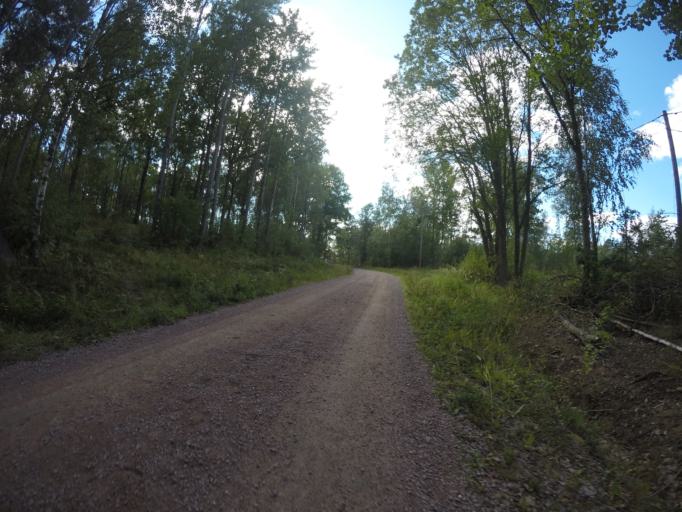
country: SE
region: Vaestmanland
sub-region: Hallstahammars Kommun
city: Kolback
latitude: 59.4944
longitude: 16.2097
